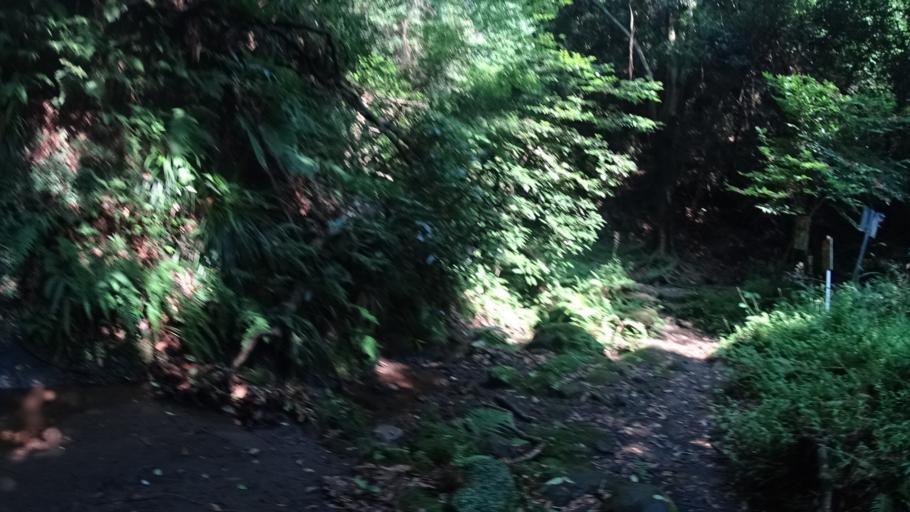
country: JP
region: Kanagawa
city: Zushi
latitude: 35.3053
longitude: 139.6052
